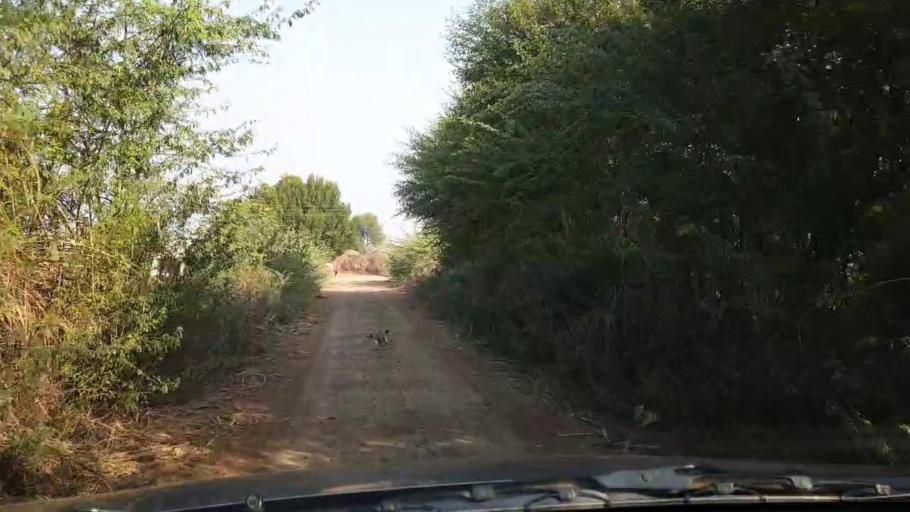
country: PK
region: Sindh
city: Sanghar
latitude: 25.9864
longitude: 68.9497
